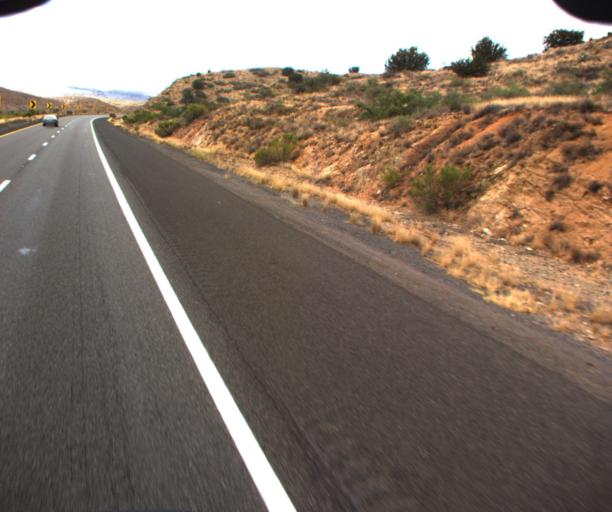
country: US
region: Arizona
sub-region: Yavapai County
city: Cordes Lakes
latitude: 34.2746
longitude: -112.1157
